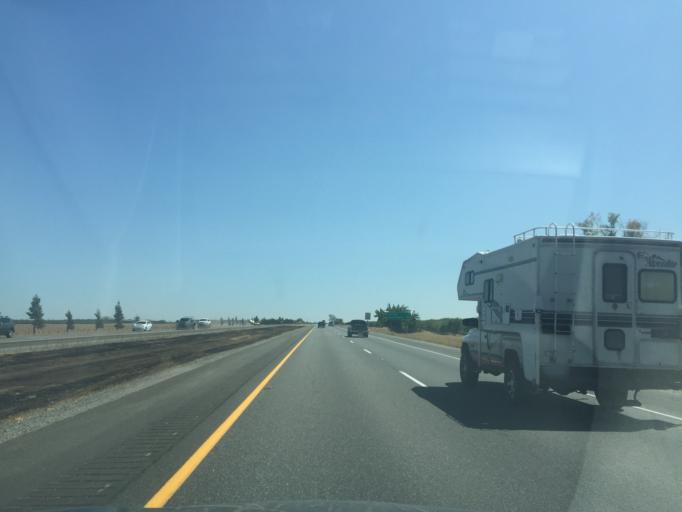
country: US
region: California
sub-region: Tehama County
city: Corning
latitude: 39.9929
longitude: -122.2048
